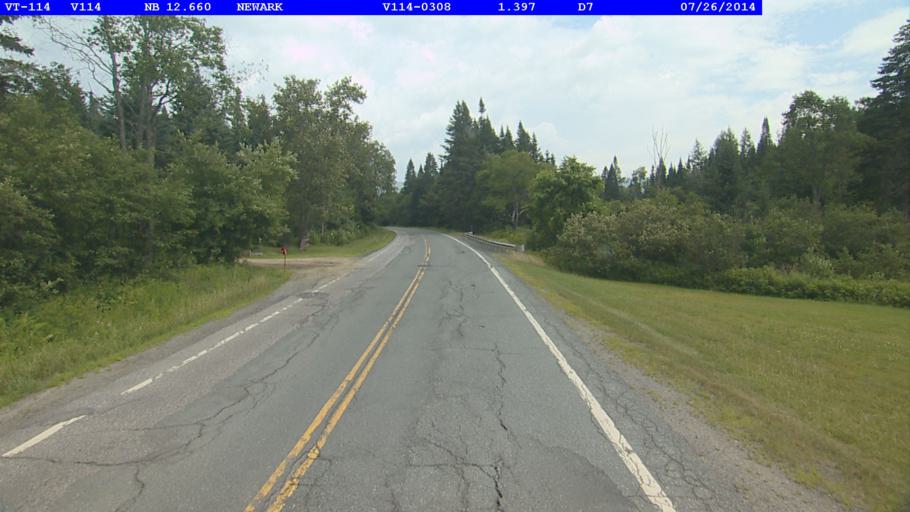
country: US
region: Vermont
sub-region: Caledonia County
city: Lyndonville
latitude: 44.6882
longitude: -71.8750
